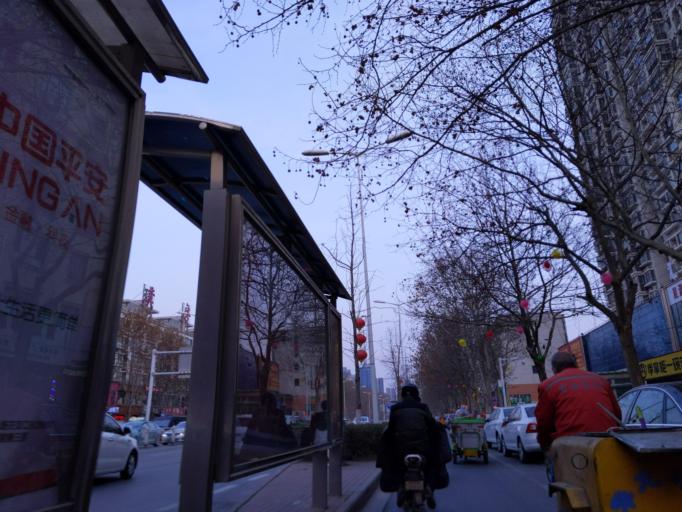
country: CN
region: Henan Sheng
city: Puyang
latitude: 35.7805
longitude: 115.0336
